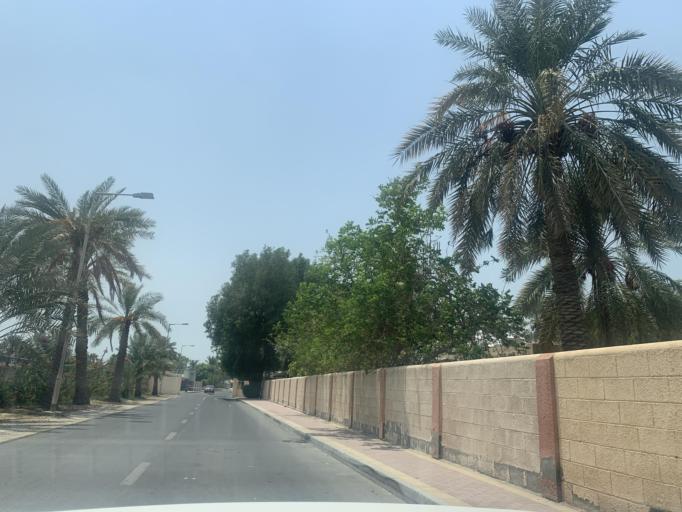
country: BH
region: Central Governorate
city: Madinat Hamad
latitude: 26.1343
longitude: 50.4612
